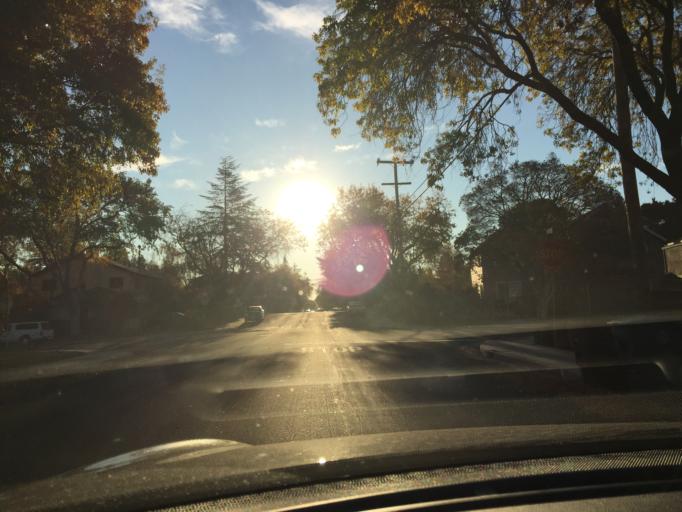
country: US
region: California
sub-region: Santa Clara County
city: Palo Alto
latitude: 37.4340
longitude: -122.1240
